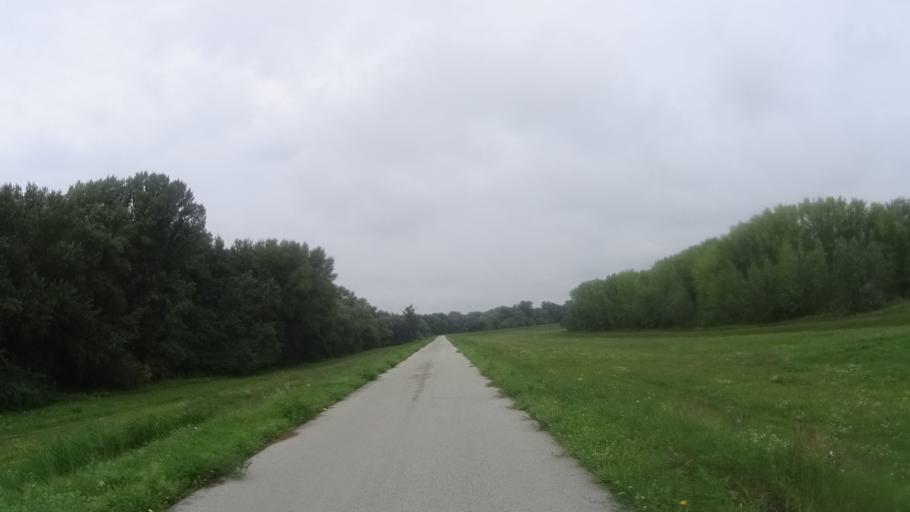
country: SK
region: Nitriansky
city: Komarno
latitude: 47.7517
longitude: 18.1512
